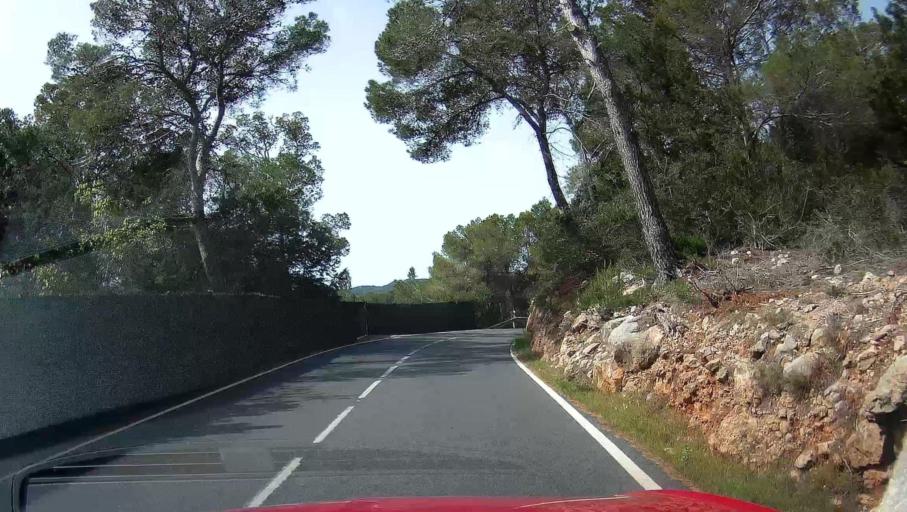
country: ES
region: Balearic Islands
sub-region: Illes Balears
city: Sant Joan de Labritja
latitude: 39.0642
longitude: 1.5868
